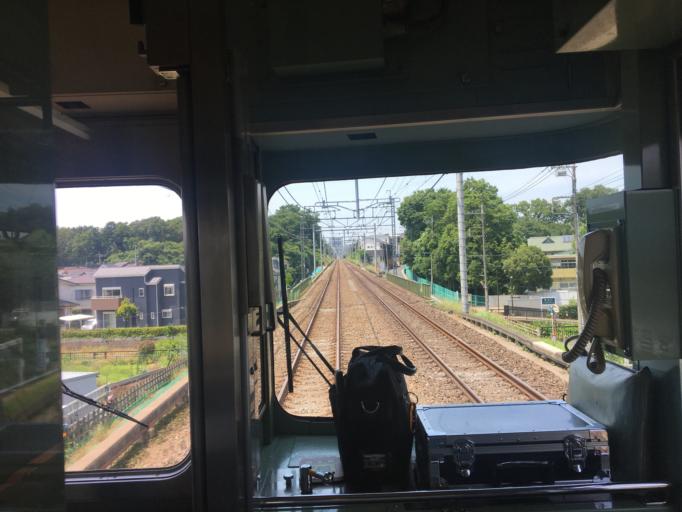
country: JP
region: Tokyo
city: Tanashicho
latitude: 35.7633
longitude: 139.5310
